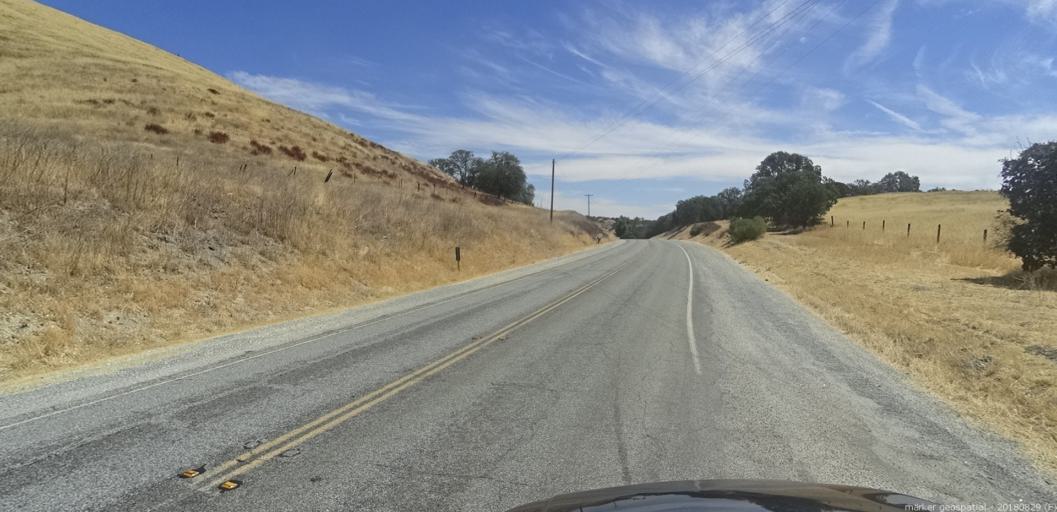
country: US
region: California
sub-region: San Luis Obispo County
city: Lake Nacimiento
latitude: 35.9083
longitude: -121.0131
